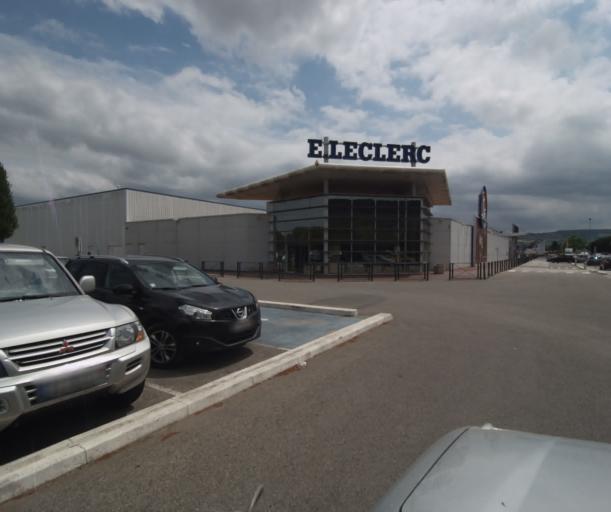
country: FR
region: Languedoc-Roussillon
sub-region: Departement de l'Aude
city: Limoux
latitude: 43.0747
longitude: 2.2226
